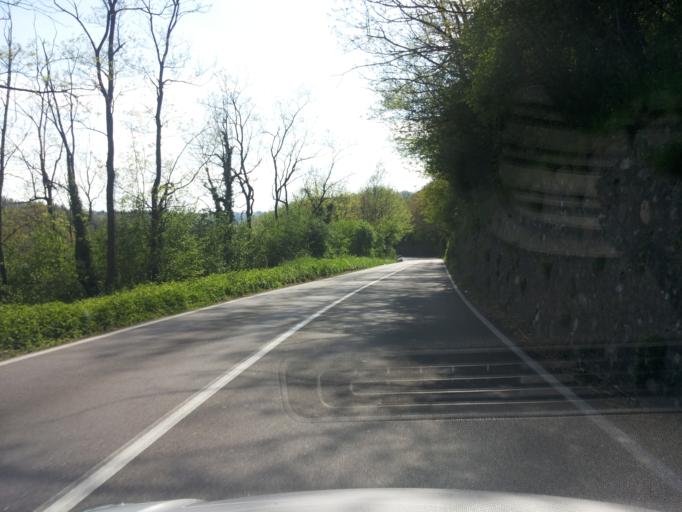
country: IT
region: Lombardy
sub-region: Provincia di Varese
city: Malnate
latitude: 45.8063
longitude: 8.8777
